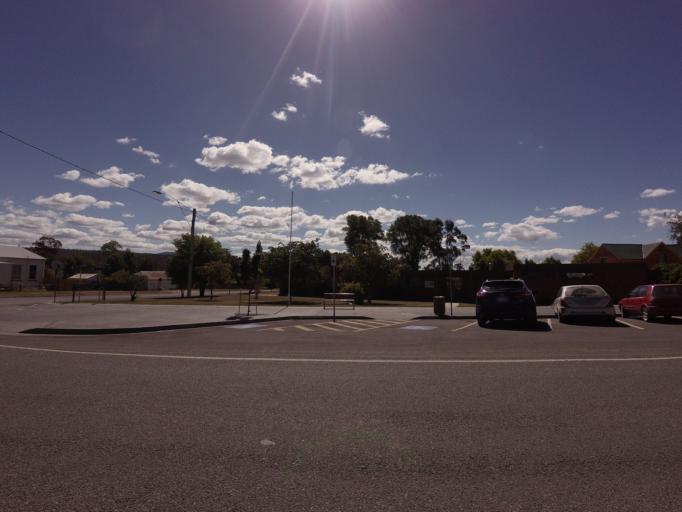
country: AU
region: Tasmania
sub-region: Break O'Day
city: St Helens
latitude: -41.6382
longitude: 147.9699
